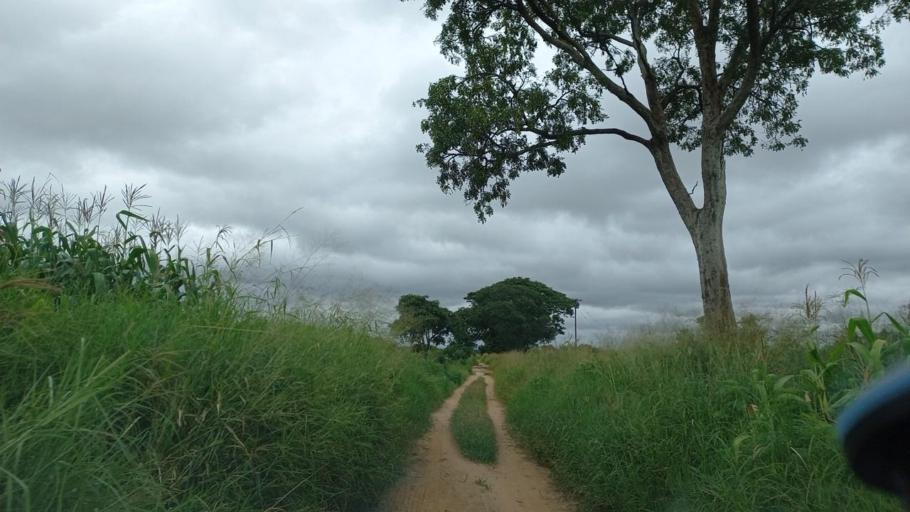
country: ZM
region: Lusaka
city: Lusaka
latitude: -15.1187
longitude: 28.3726
